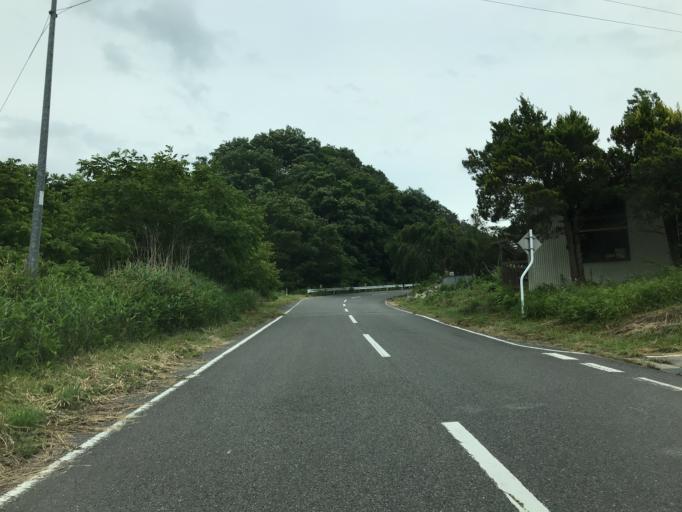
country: JP
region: Fukushima
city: Funehikimachi-funehiki
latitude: 37.3877
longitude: 140.5390
